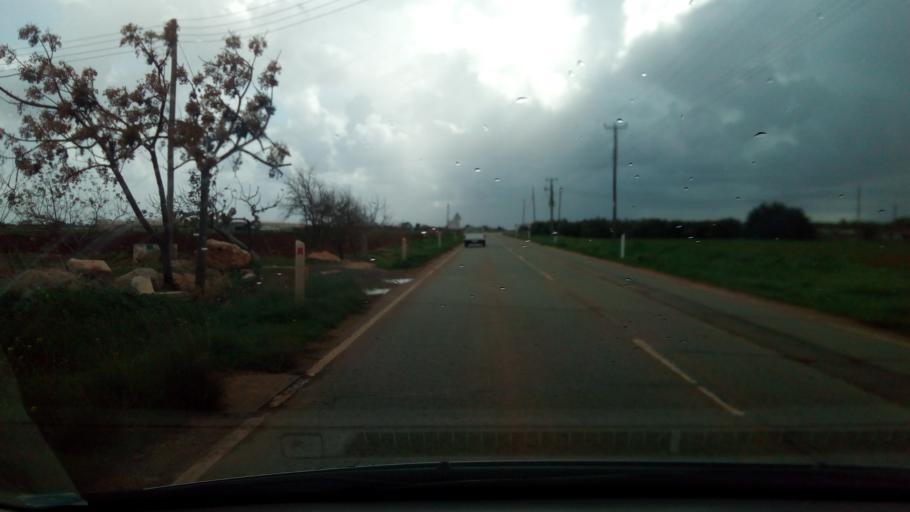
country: CY
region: Ammochostos
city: Liopetri
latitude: 34.9879
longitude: 33.8936
